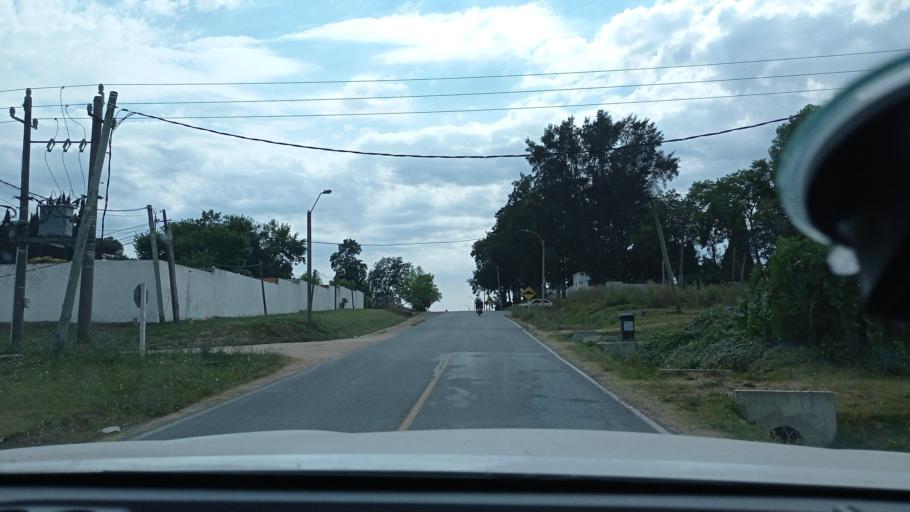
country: UY
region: Canelones
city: Pando
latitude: -34.7110
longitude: -55.9688
